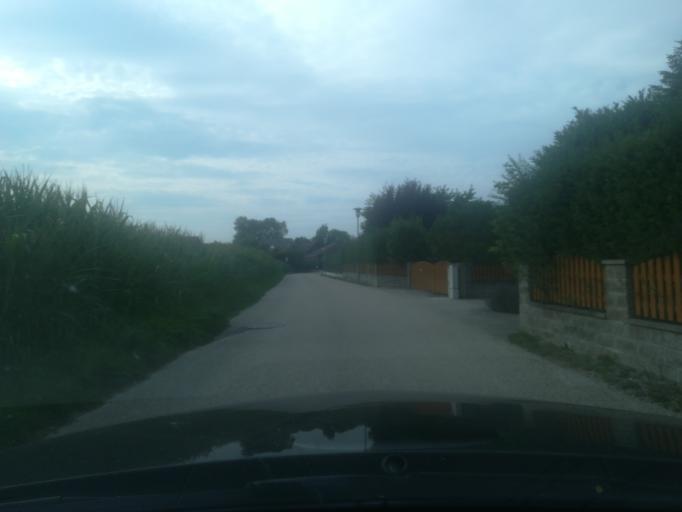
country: AT
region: Upper Austria
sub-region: Wels-Land
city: Marchtrenk
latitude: 48.1854
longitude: 14.1325
